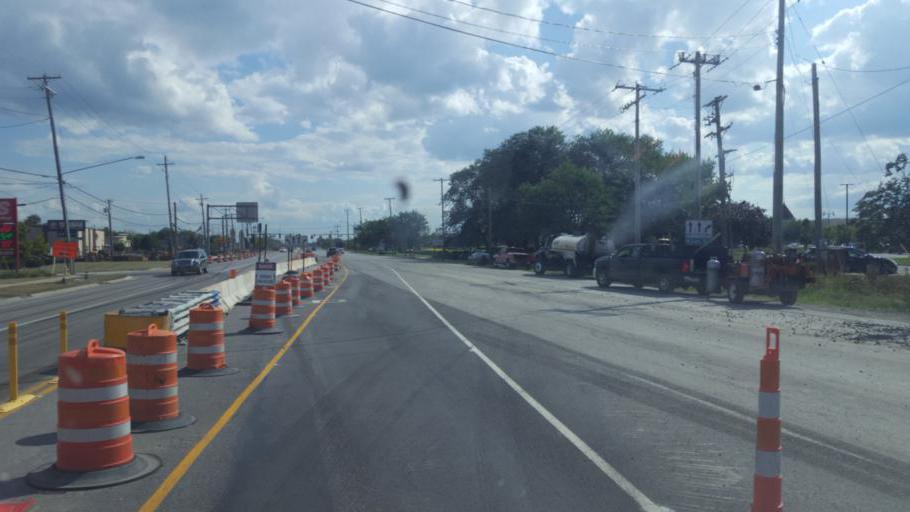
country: US
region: Ohio
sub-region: Wood County
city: Perrysburg
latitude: 41.5298
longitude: -83.6366
